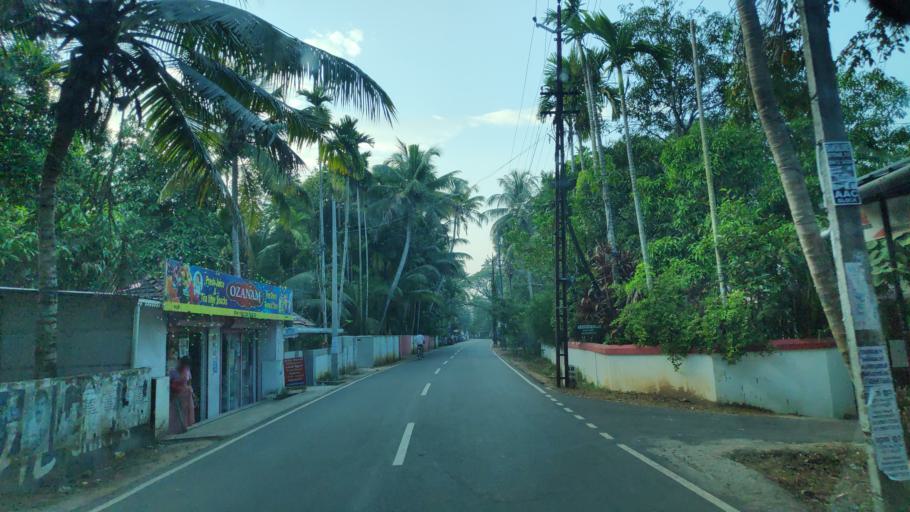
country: IN
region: Kerala
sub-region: Alappuzha
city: Shertallai
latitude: 9.6779
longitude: 76.3777
